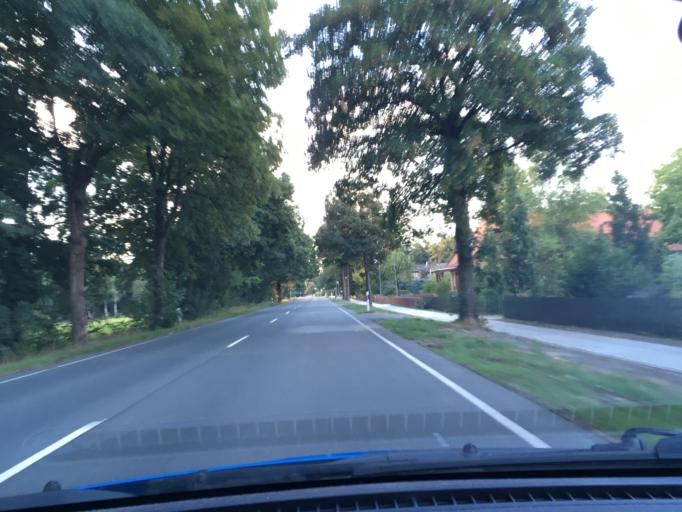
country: DE
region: Lower Saxony
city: Bergen
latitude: 52.7373
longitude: 9.9765
